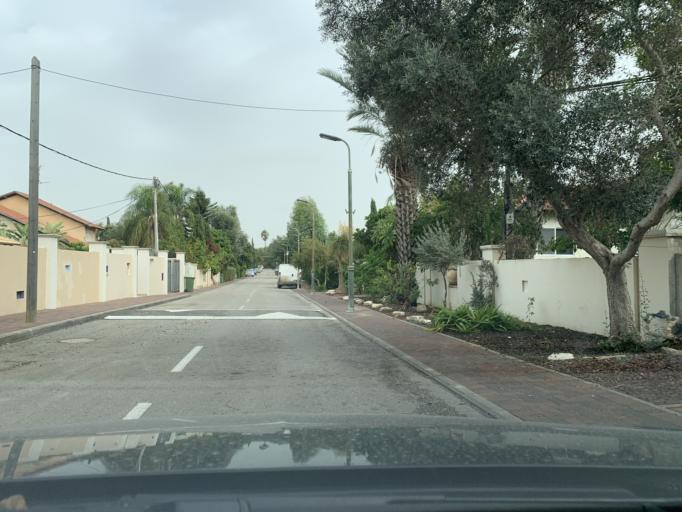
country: IL
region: Central District
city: Jaljulya
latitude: 32.1603
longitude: 34.9410
